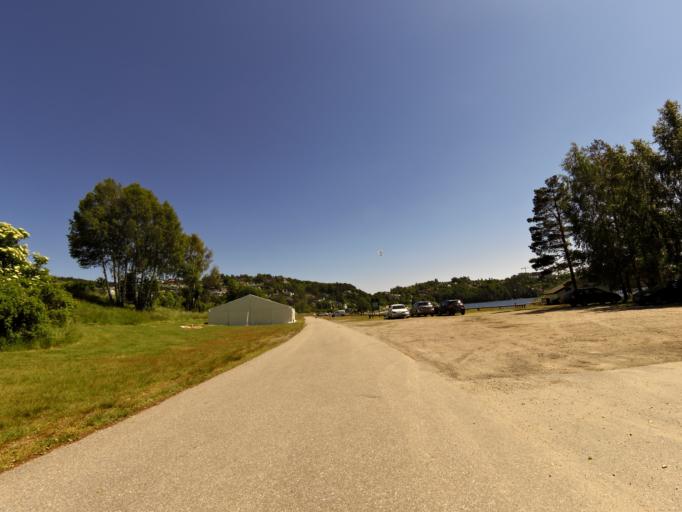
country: NO
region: Vest-Agder
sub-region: Kristiansand
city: Justvik
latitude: 58.1914
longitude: 8.0812
